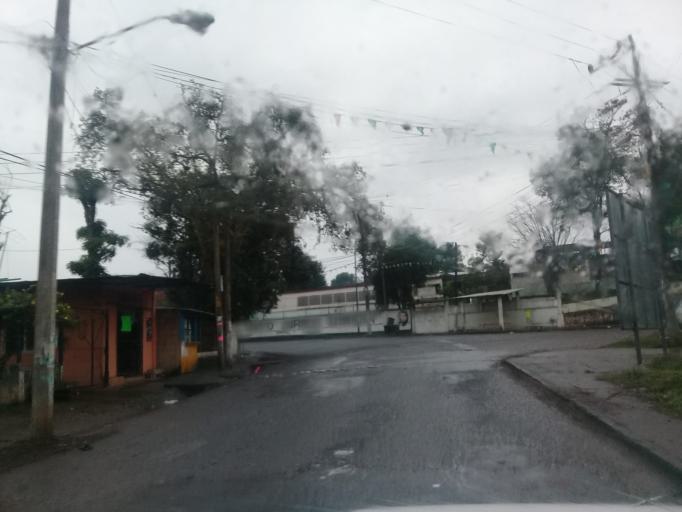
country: MX
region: Veracruz
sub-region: Cordoba
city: San Jose de Tapia
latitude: 18.8470
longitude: -96.9528
